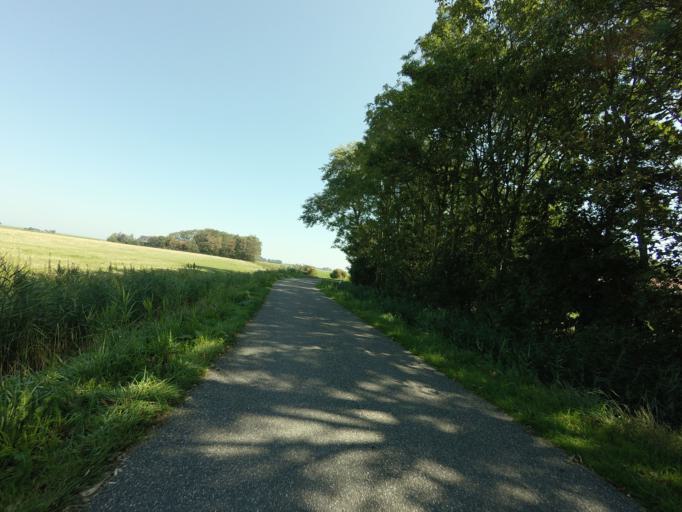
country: NL
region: Friesland
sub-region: Gemeente Dongeradeel
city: Holwerd
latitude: 53.3666
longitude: 5.9248
